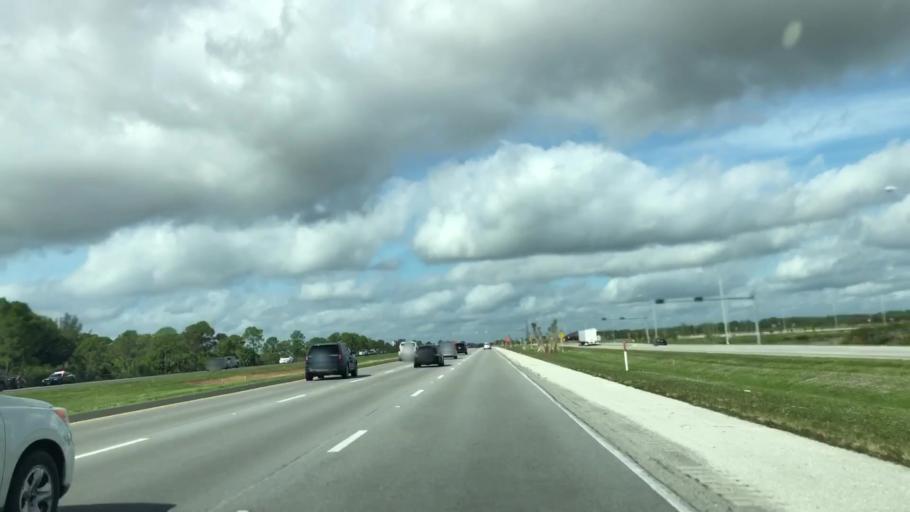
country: US
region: Florida
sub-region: Palm Beach County
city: Tequesta
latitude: 27.0018
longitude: -80.2018
